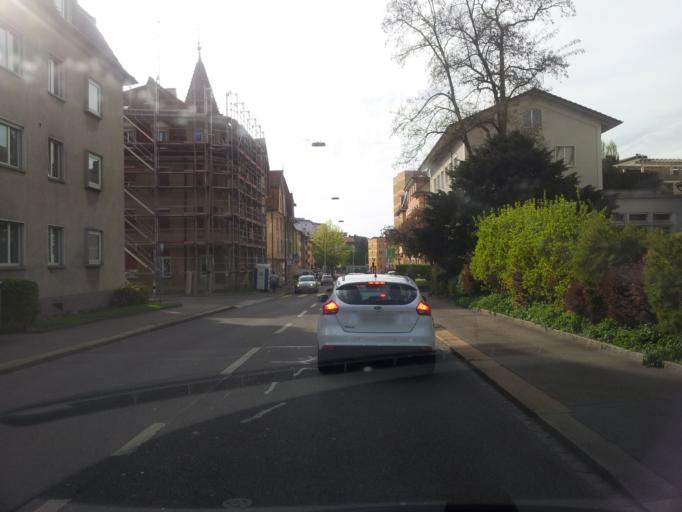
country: CH
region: Zurich
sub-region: Bezirk Zuerich
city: Zuerich (Kreis 11) / Oerlikon
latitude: 47.4064
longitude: 8.5520
